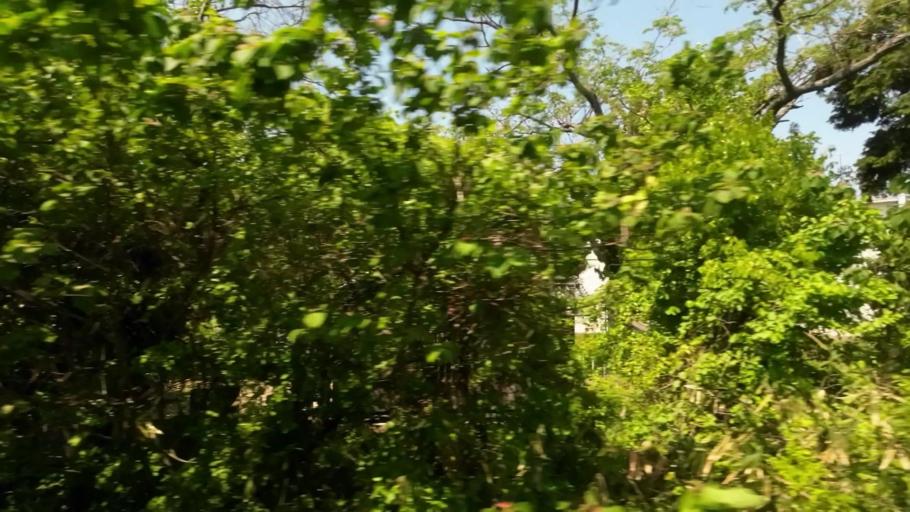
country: JP
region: Ehime
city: Hojo
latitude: 34.0711
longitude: 132.9324
